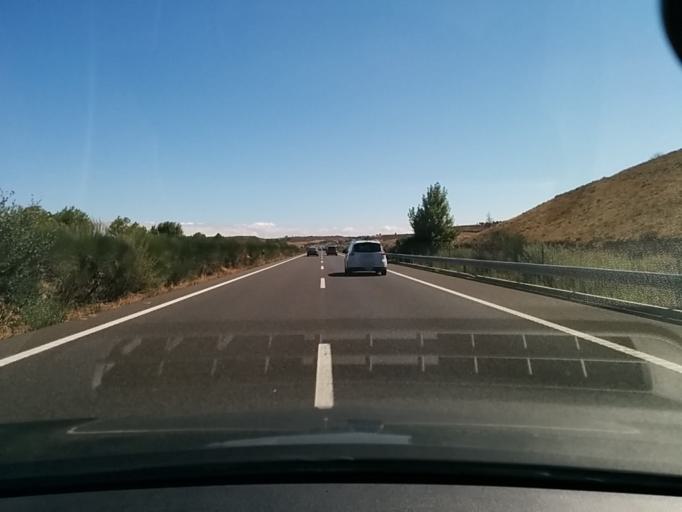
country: ES
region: Aragon
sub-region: Provincia de Huesca
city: Almudebar
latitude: 42.0485
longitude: -0.5565
